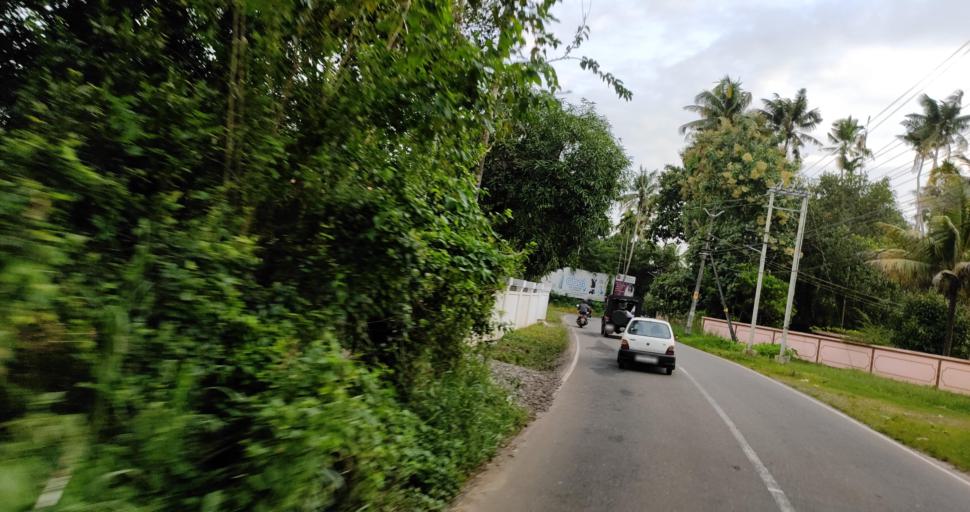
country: IN
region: Kerala
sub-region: Thrissur District
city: Kizhake Chalakudi
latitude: 10.3175
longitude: 76.3560
